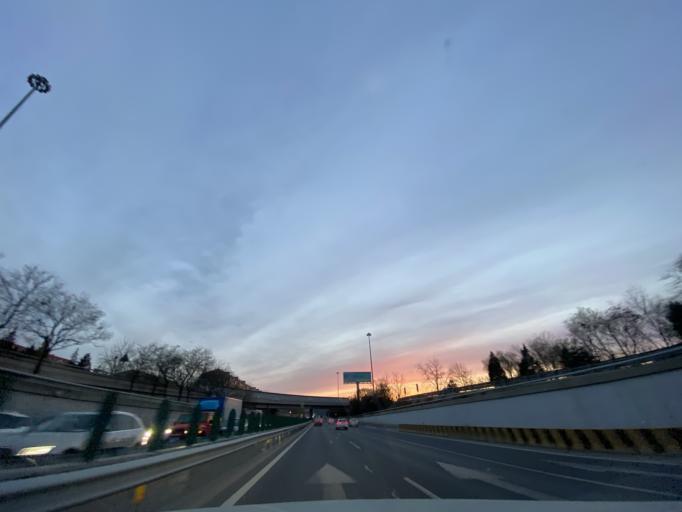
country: CN
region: Beijing
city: Haidian
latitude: 40.0120
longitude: 116.2794
